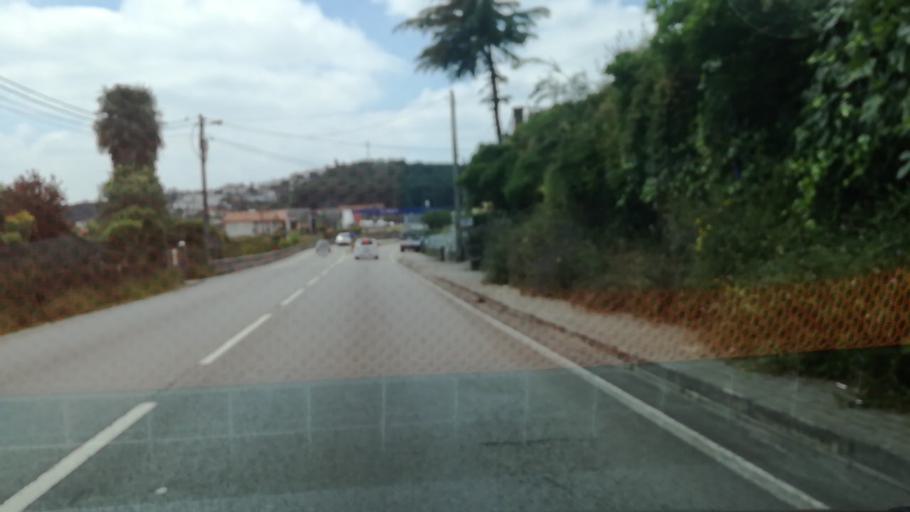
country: PT
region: Braga
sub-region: Vila Nova de Famalicao
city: Calendario
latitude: 41.3894
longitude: -8.5276
